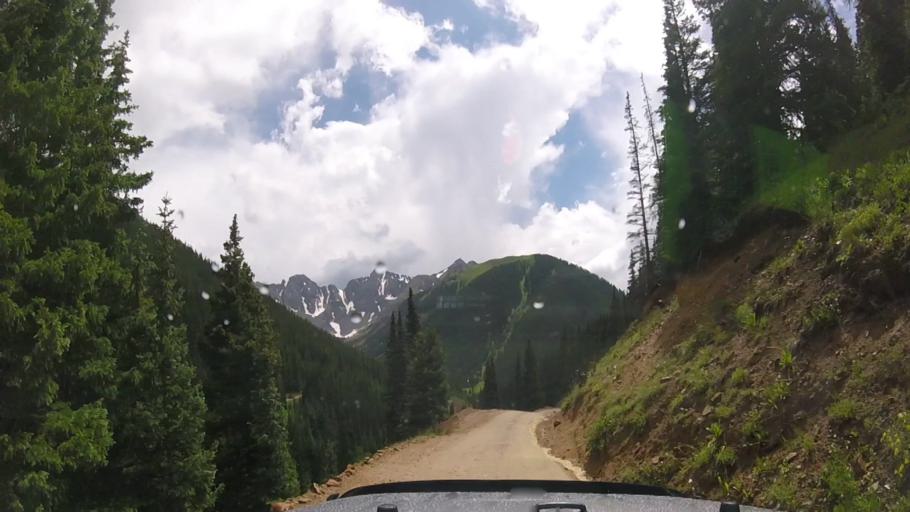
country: US
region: Colorado
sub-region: San Juan County
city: Silverton
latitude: 37.8953
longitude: -107.6477
